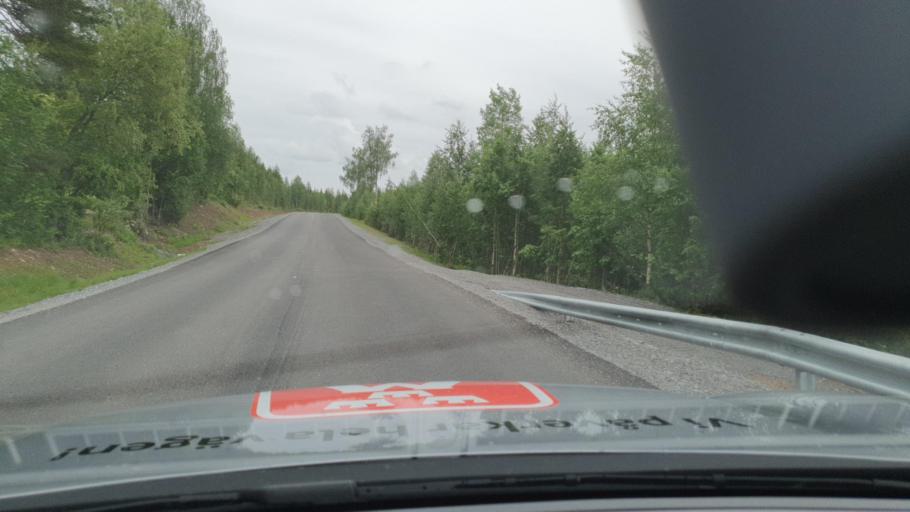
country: SE
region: Norrbotten
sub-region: Overtornea Kommun
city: OEvertornea
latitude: 66.5934
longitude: 23.3123
